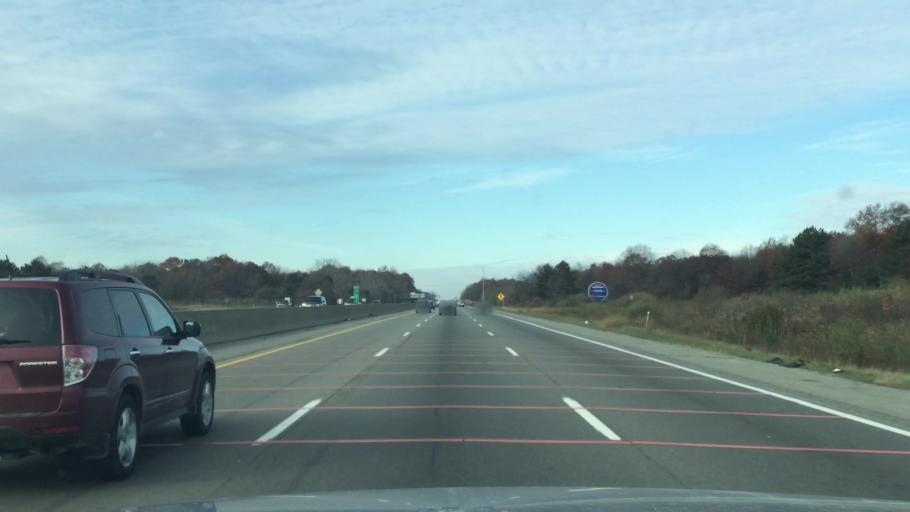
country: US
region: Michigan
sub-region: Washtenaw County
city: Ypsilanti
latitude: 42.2244
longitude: -83.6532
